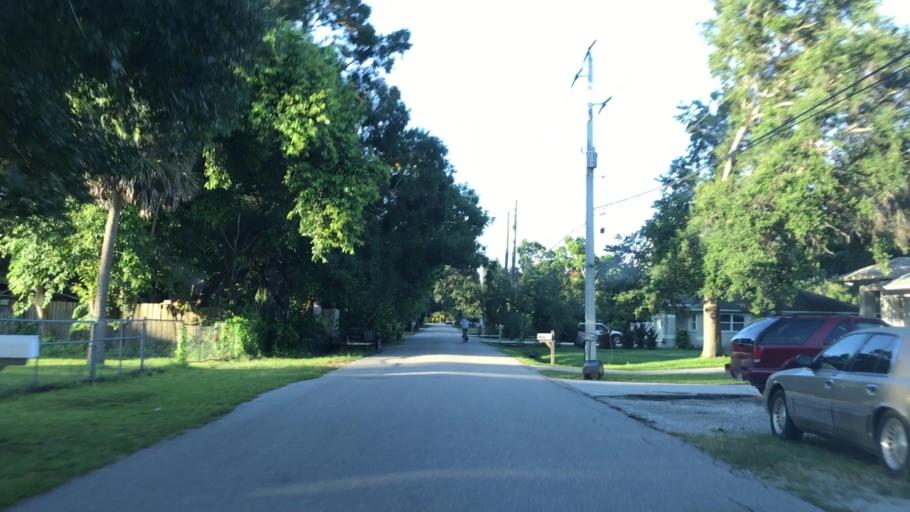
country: US
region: Florida
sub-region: Sarasota County
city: Fruitville
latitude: 27.3256
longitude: -82.4593
